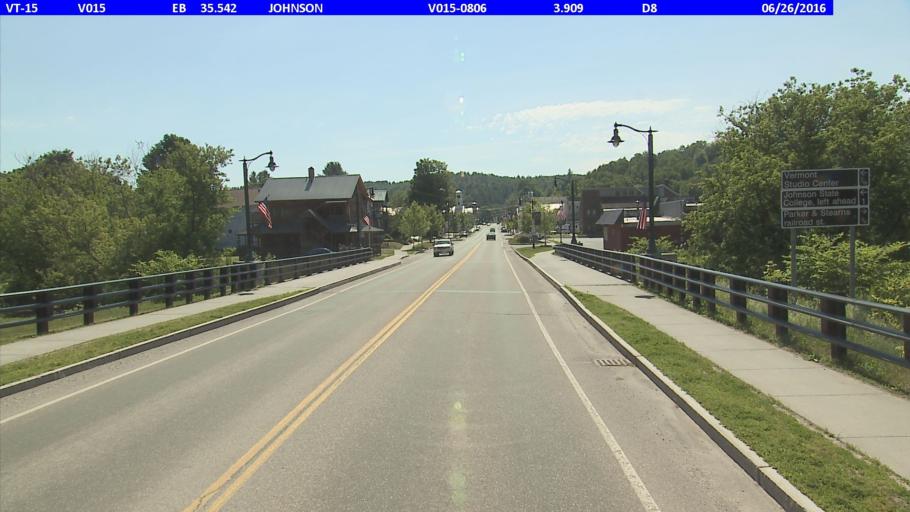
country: US
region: Vermont
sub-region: Lamoille County
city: Johnson
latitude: 44.6364
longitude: -72.6826
